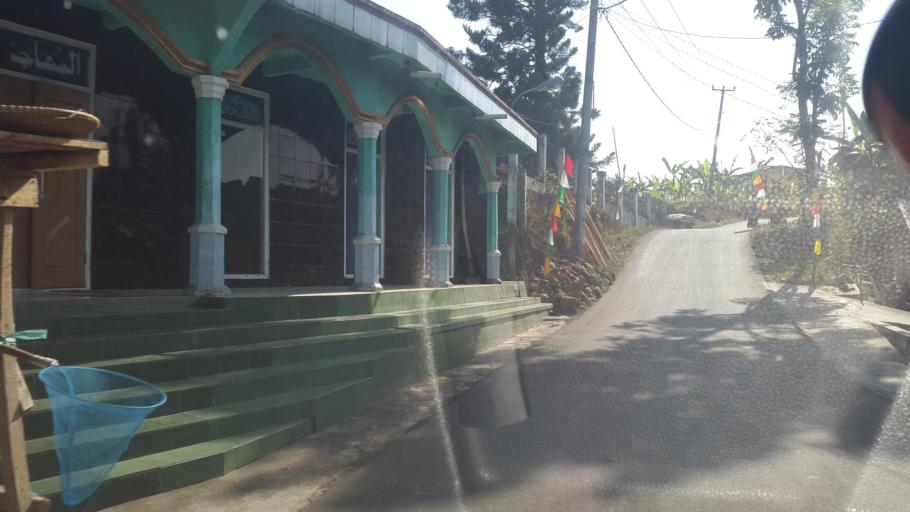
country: ID
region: West Java
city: Cicurug
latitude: -6.8208
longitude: 106.7015
